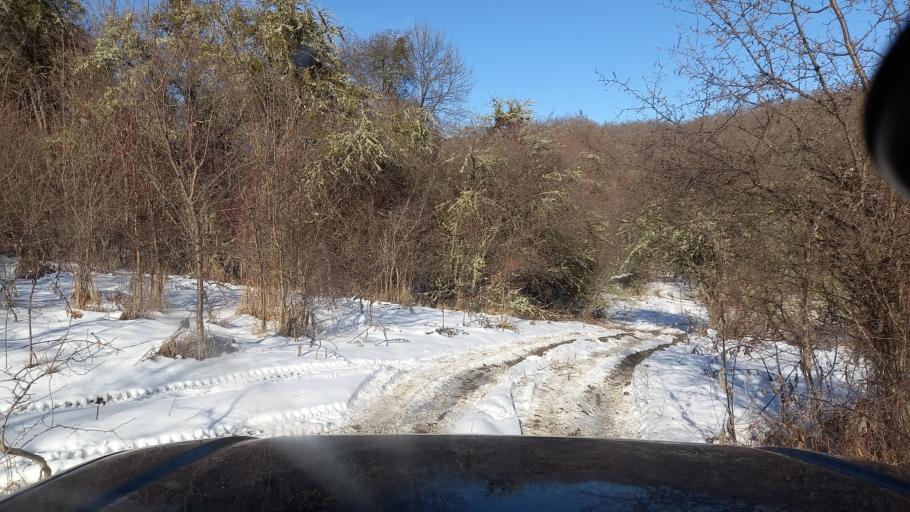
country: RU
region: Adygeya
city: Kamennomostskiy
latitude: 44.2104
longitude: 40.1440
